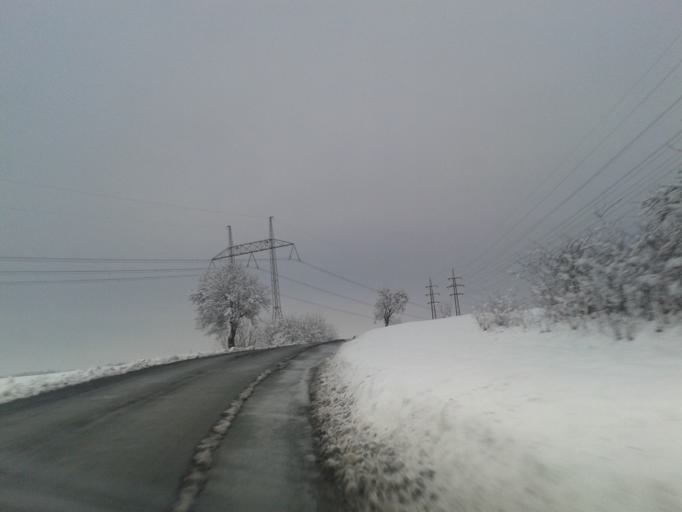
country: CZ
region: Central Bohemia
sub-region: Okres Beroun
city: Beroun
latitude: 49.9251
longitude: 14.0900
